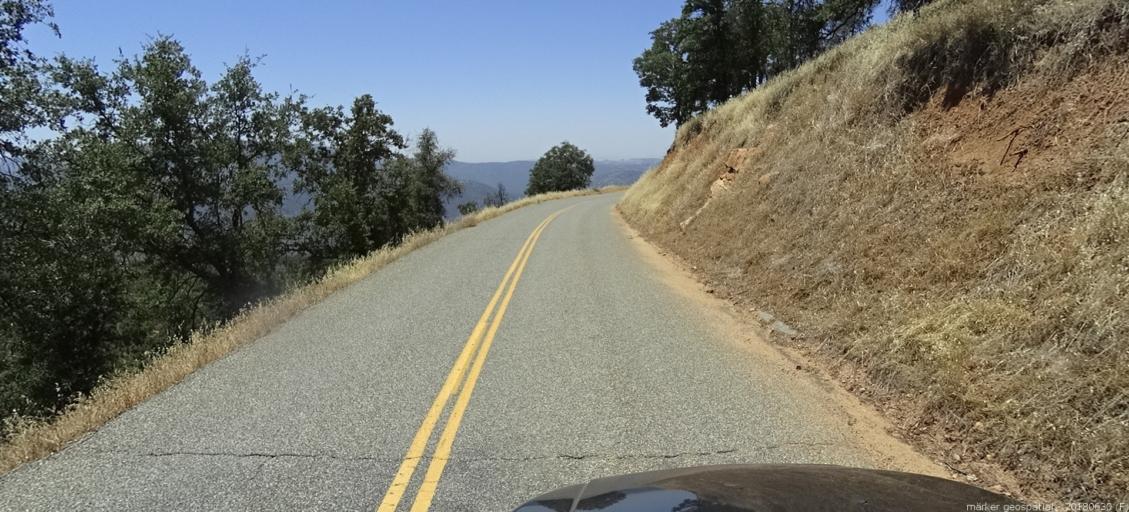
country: US
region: California
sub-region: Fresno County
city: Auberry
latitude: 37.1835
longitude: -119.4281
